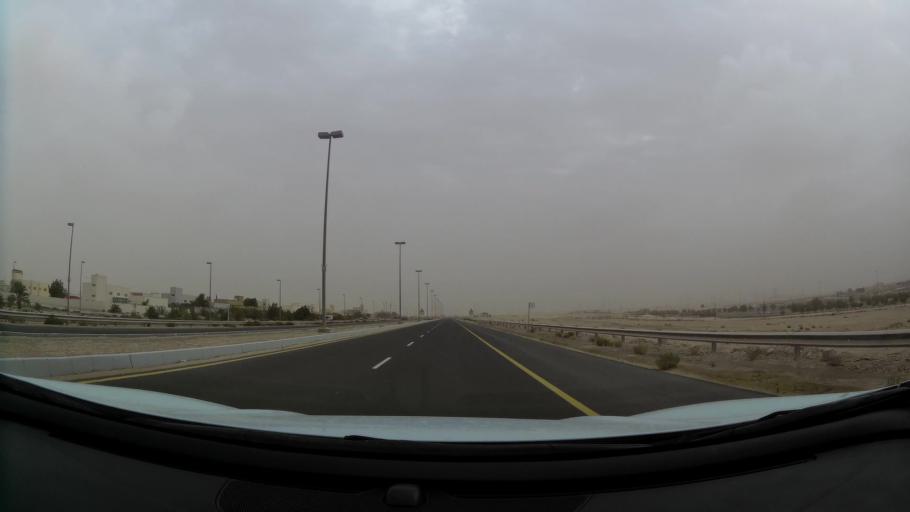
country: AE
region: Abu Dhabi
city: Abu Dhabi
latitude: 24.4212
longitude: 54.7504
